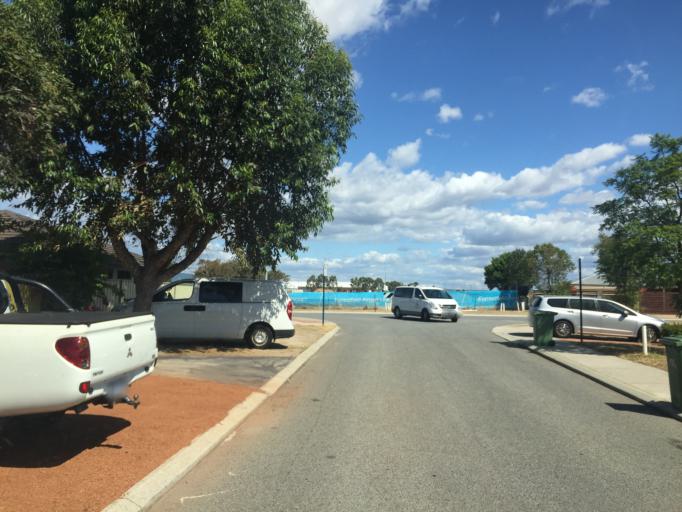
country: AU
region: Western Australia
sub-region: Belmont
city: Redcliffe
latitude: -31.9348
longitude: 115.9474
